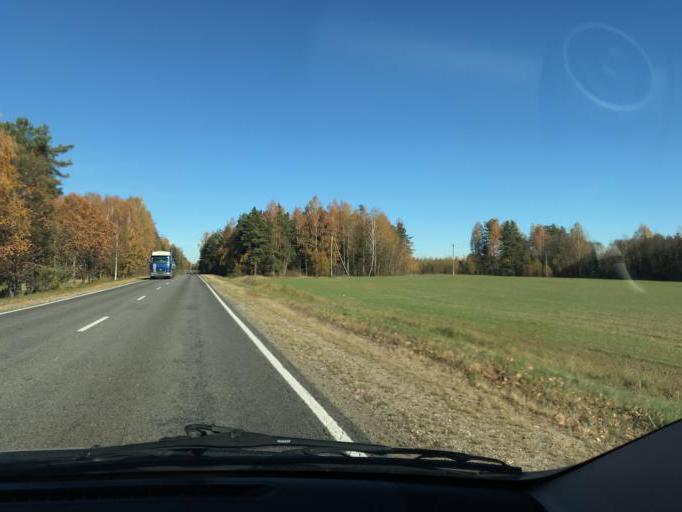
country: BY
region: Vitebsk
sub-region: Ushatski Rayon
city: Ushachy
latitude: 55.0904
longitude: 28.7566
